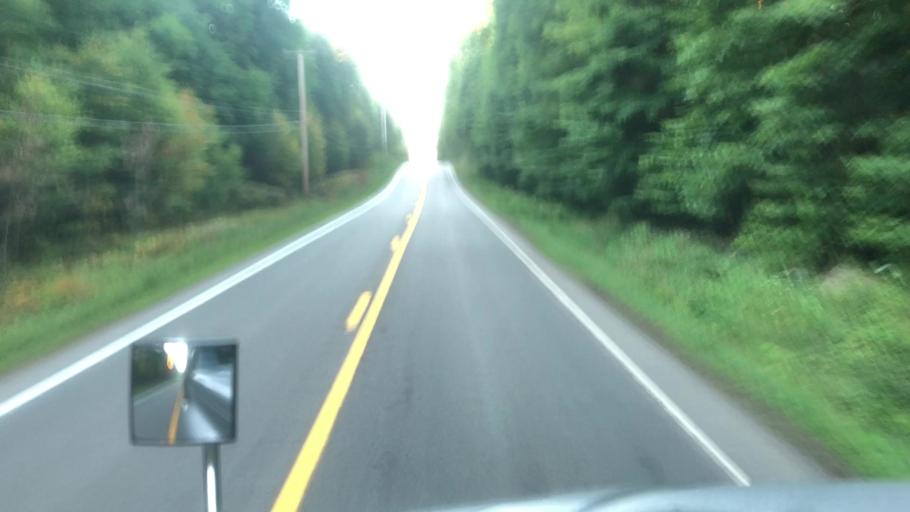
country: US
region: Pennsylvania
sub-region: Crawford County
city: Titusville
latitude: 41.5538
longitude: -79.6111
